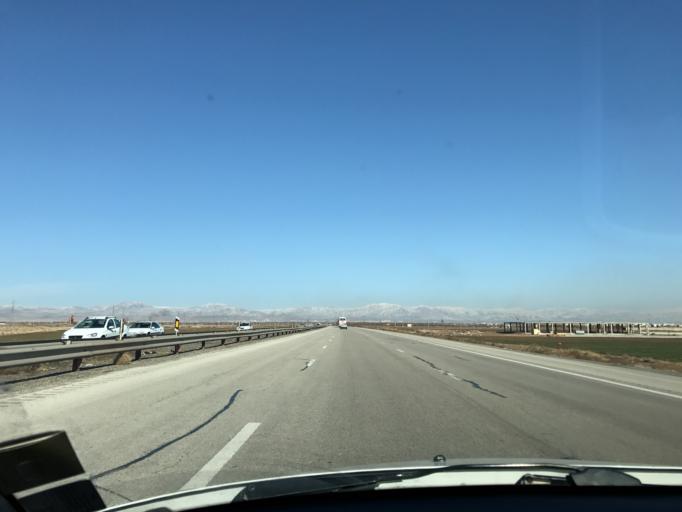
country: IR
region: Qazvin
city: Qazvin
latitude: 36.2245
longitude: 49.8897
